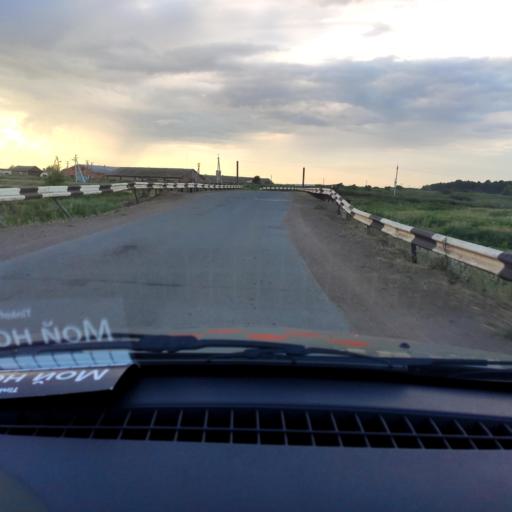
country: RU
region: Bashkortostan
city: Mikhaylovka
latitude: 54.9703
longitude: 55.7884
